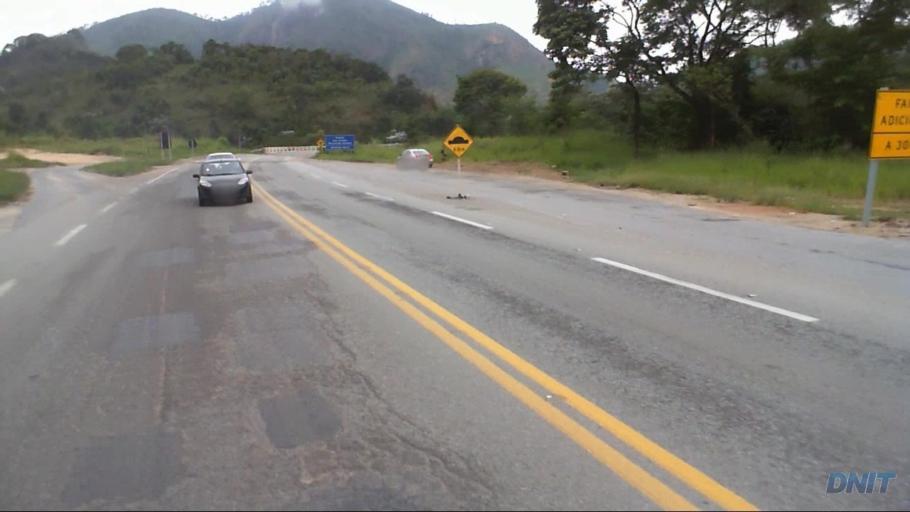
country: BR
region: Minas Gerais
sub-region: Nova Era
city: Nova Era
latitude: -19.6579
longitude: -42.9606
